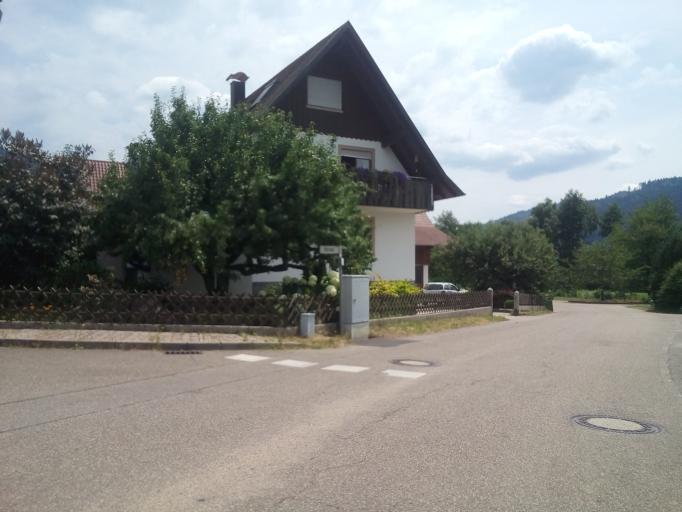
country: DE
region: Baden-Wuerttemberg
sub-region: Freiburg Region
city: Kappelrodeck
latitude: 48.5991
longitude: 8.1118
